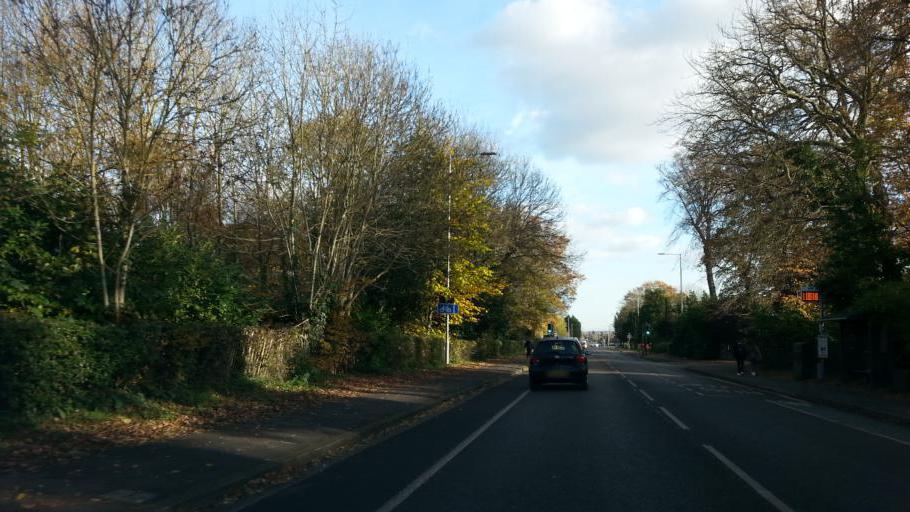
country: GB
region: England
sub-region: Wokingham
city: Earley
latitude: 51.4415
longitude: -0.9274
